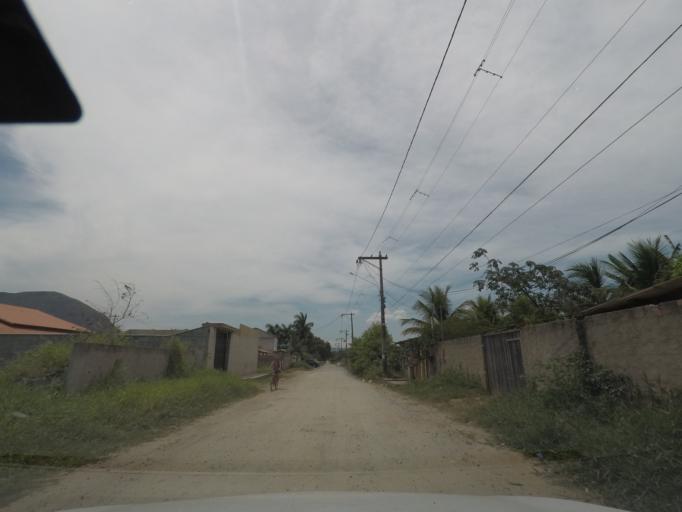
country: BR
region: Rio de Janeiro
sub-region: Marica
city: Marica
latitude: -22.9561
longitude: -42.9456
